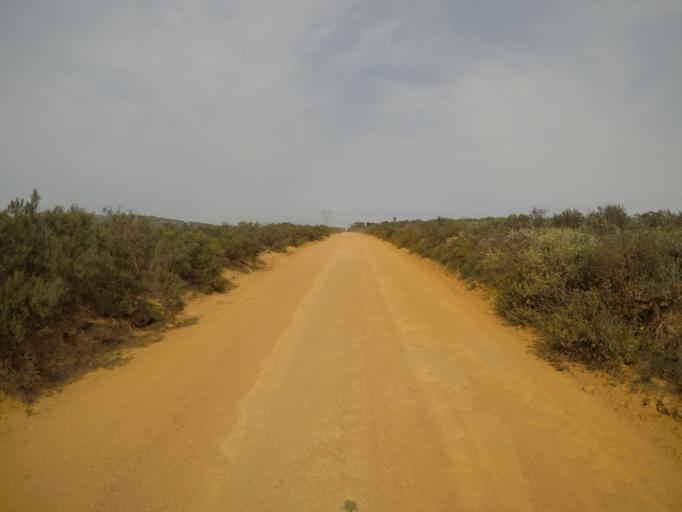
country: ZA
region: Western Cape
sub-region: West Coast District Municipality
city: Malmesbury
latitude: -33.4517
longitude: 18.7444
